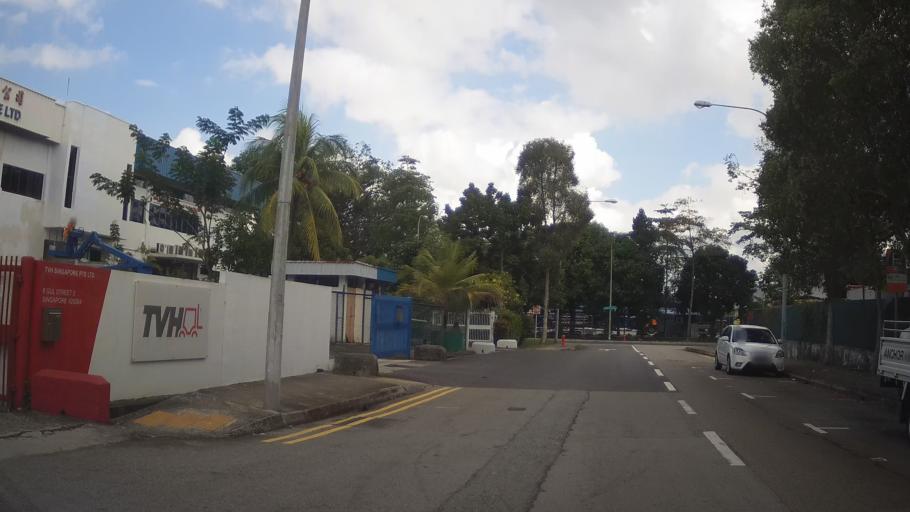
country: MY
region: Johor
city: Johor Bahru
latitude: 1.3189
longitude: 103.6675
